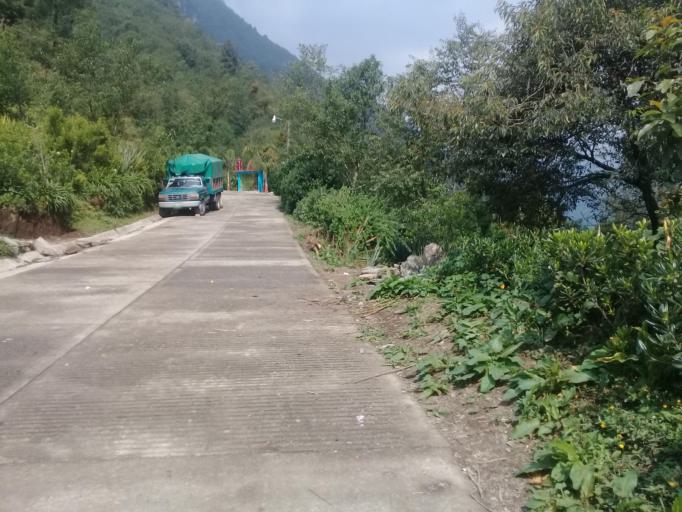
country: MX
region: Veracruz
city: La Perla
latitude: 18.9439
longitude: -97.1584
